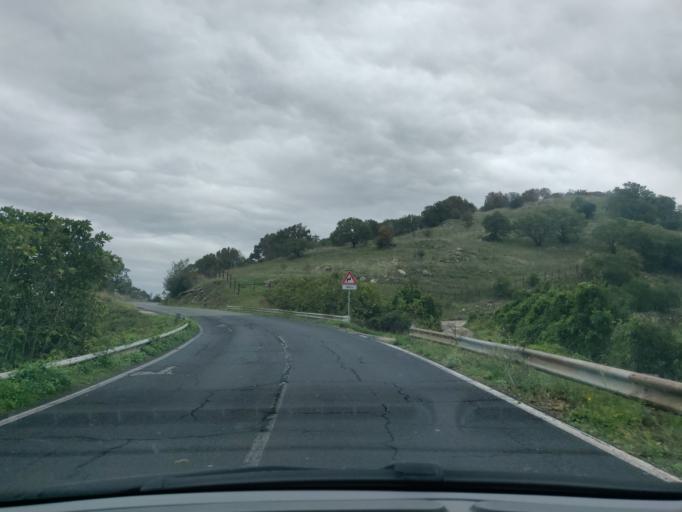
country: IT
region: Latium
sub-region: Citta metropolitana di Roma Capitale
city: Allumiere
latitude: 42.1433
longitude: 11.8793
